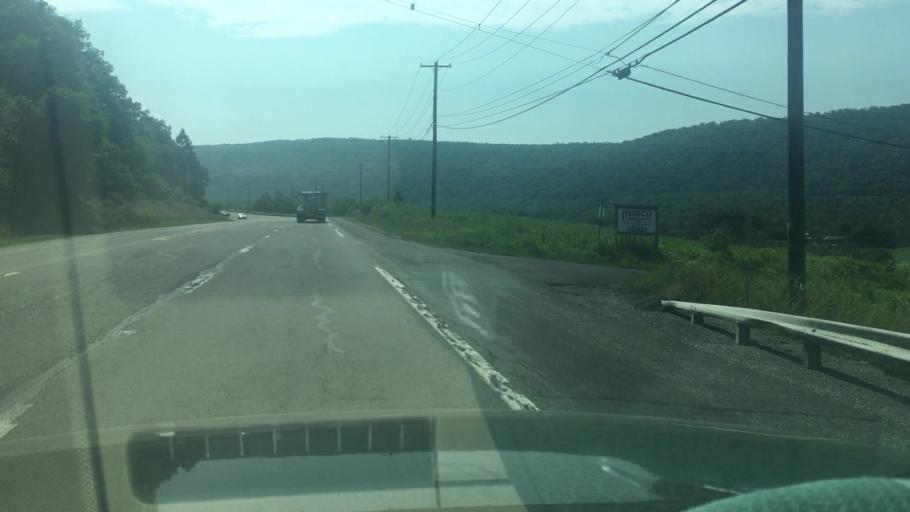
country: US
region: Pennsylvania
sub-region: Schuylkill County
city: Ashland
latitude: 40.7247
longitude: -76.3885
